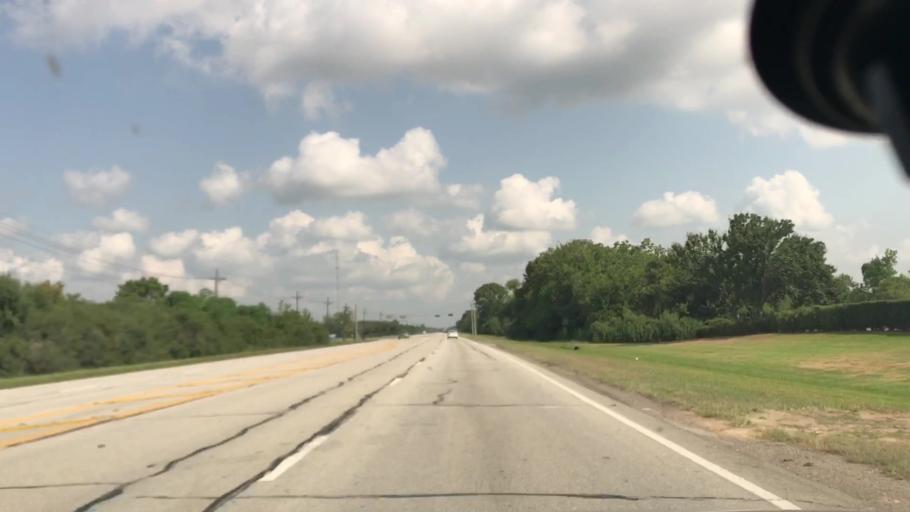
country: US
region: Texas
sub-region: Brazoria County
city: Angleton
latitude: 29.2068
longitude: -95.4360
